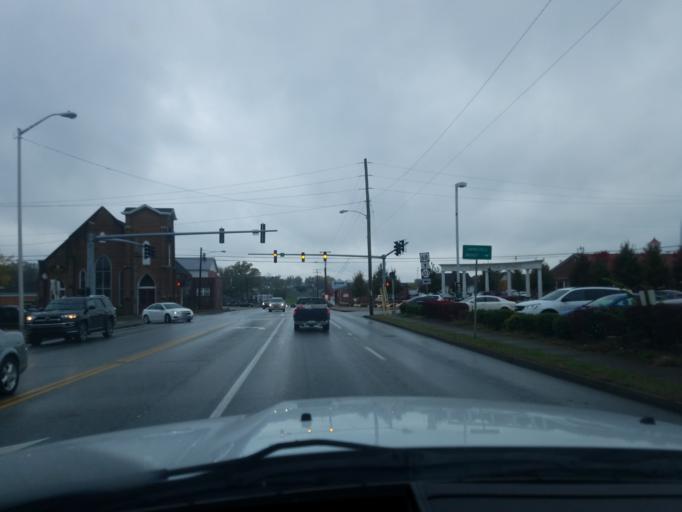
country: US
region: Kentucky
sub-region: Taylor County
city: Campbellsville
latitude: 37.3417
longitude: -85.3453
